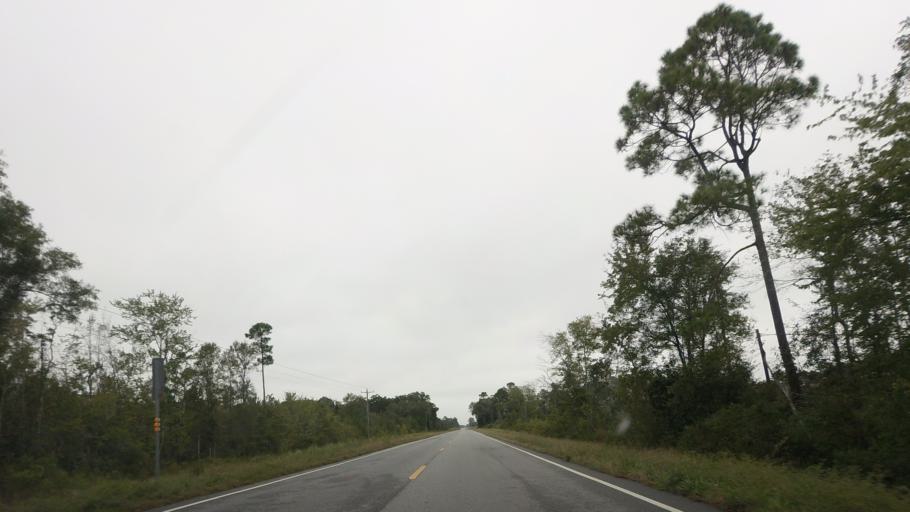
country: US
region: Georgia
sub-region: Berrien County
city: Enigma
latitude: 31.3396
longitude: -83.2291
